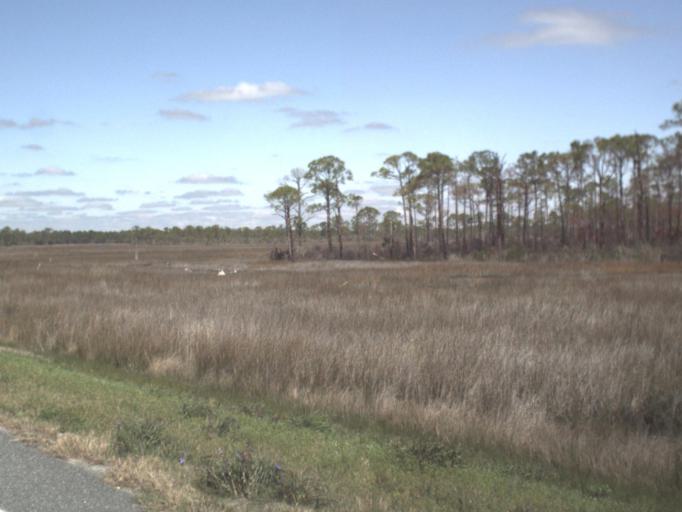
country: US
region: Florida
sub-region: Wakulla County
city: Crawfordville
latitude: 29.9860
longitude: -84.3871
